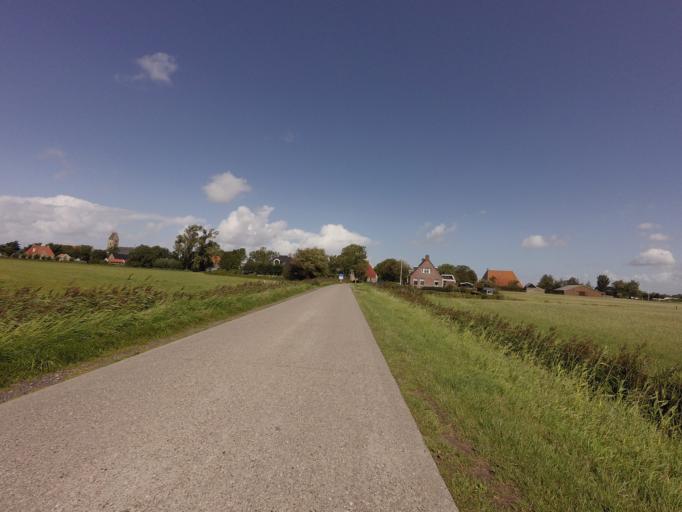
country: NL
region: Friesland
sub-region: Sudwest Fryslan
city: Makkum
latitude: 53.0787
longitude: 5.4524
